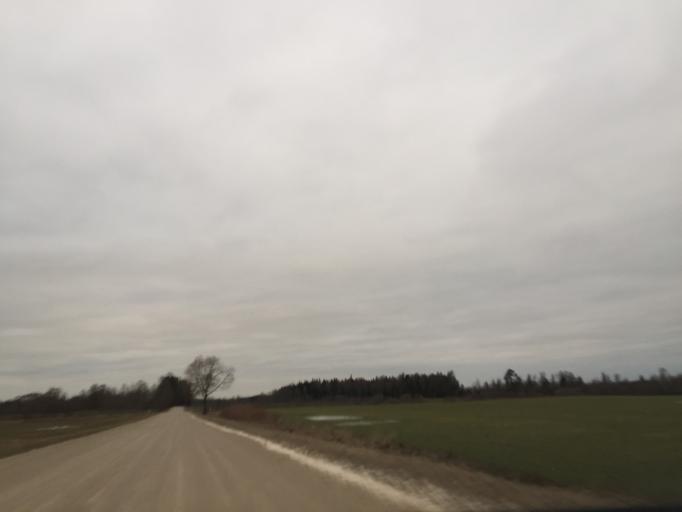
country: LT
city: Zagare
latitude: 56.2807
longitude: 23.2595
